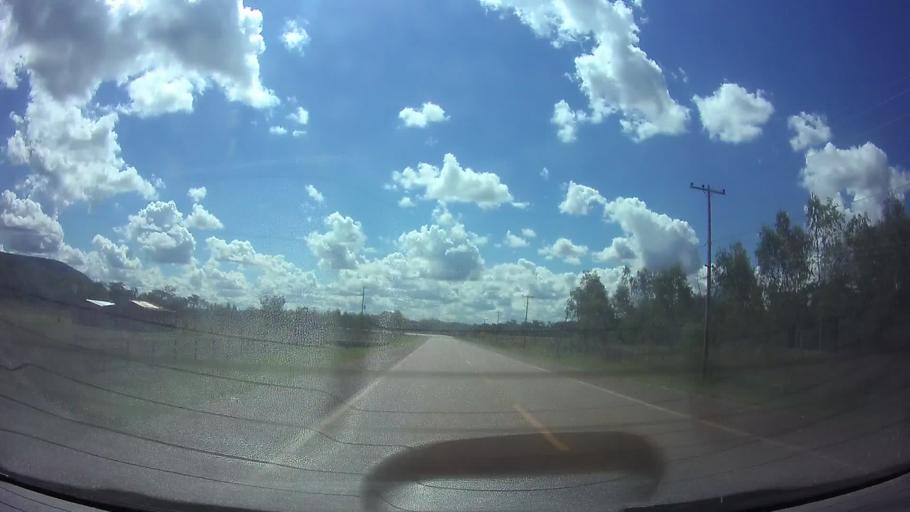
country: PY
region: Guaira
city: Itape
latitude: -25.9156
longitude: -56.7080
